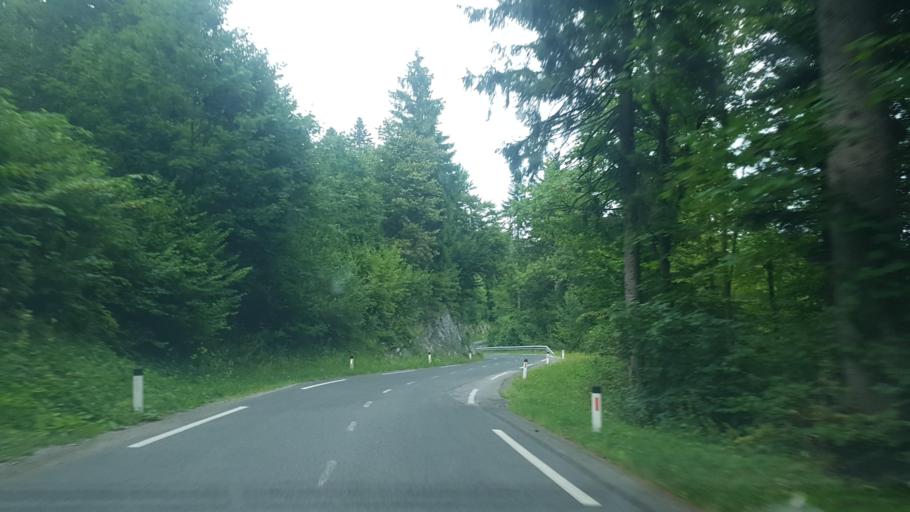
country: SI
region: Logatec
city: Logatec
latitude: 45.8671
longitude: 14.1234
